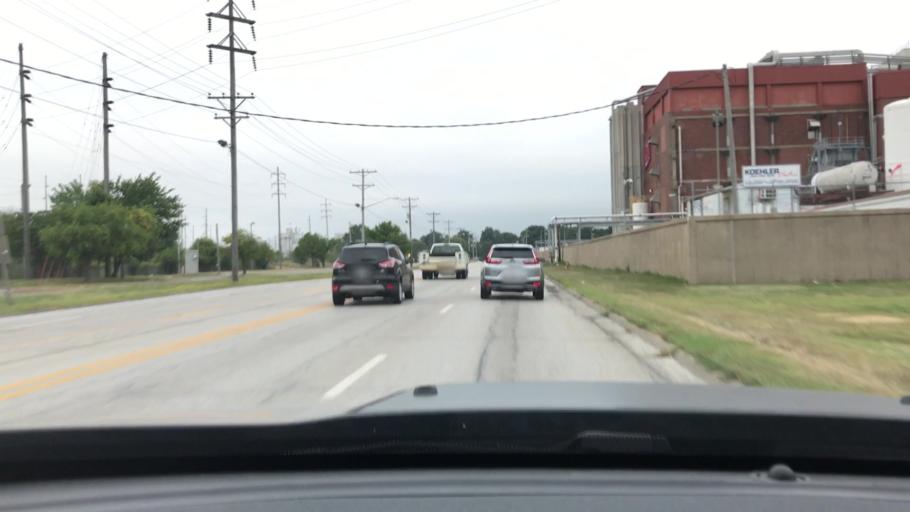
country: US
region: Iowa
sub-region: Scott County
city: Davenport
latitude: 41.5199
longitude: -90.5915
